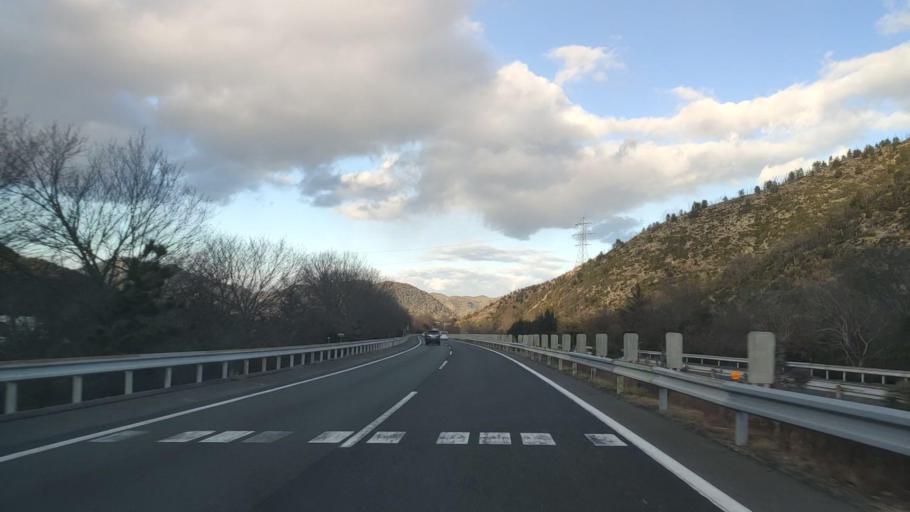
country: JP
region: Hyogo
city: Kariya
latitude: 34.7819
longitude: 134.3968
